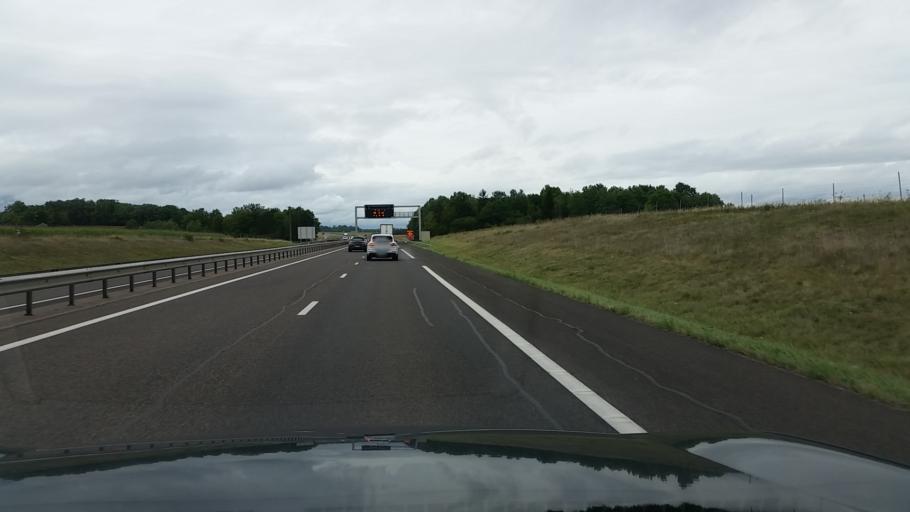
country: FR
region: Lorraine
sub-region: Departement de Meurthe-et-Moselle
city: Blenod-les-Toul
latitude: 48.6100
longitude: 5.8863
